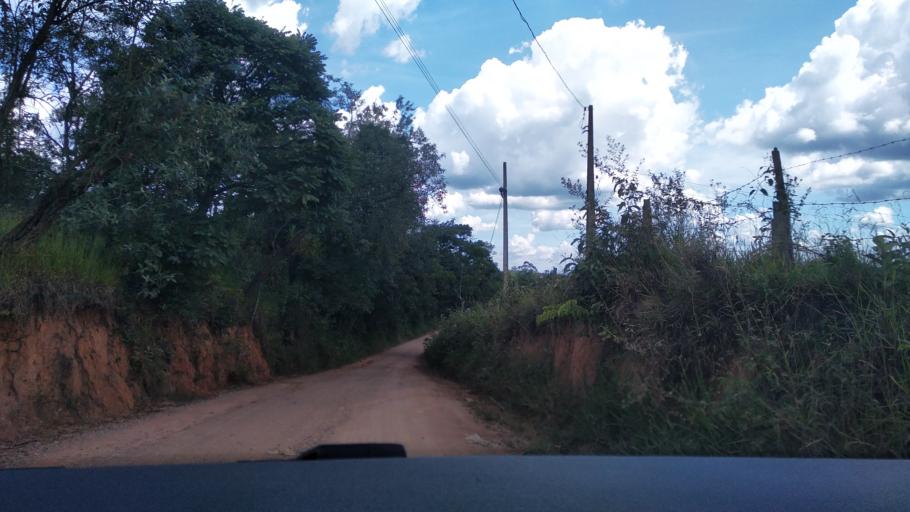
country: BR
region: Sao Paulo
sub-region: Cajamar
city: Cajamar
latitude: -23.2816
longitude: -46.8867
